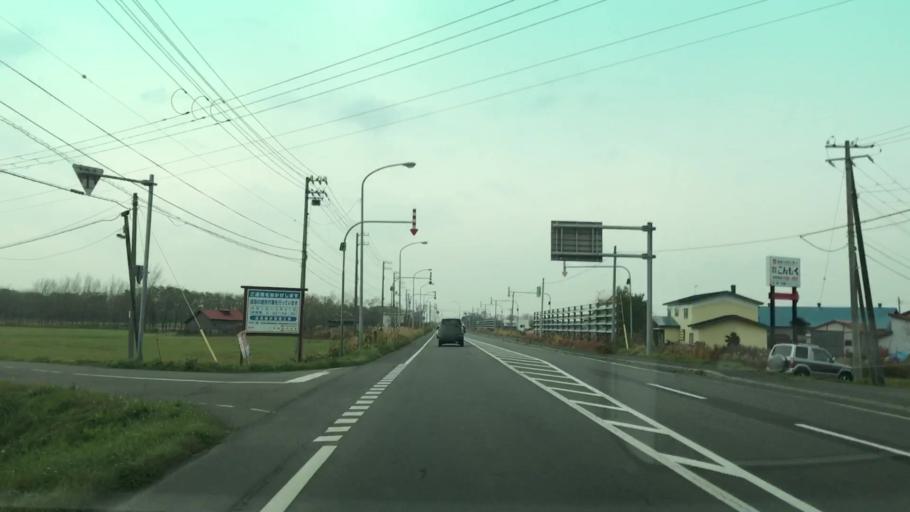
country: JP
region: Hokkaido
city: Ishikari
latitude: 43.2432
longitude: 141.3700
